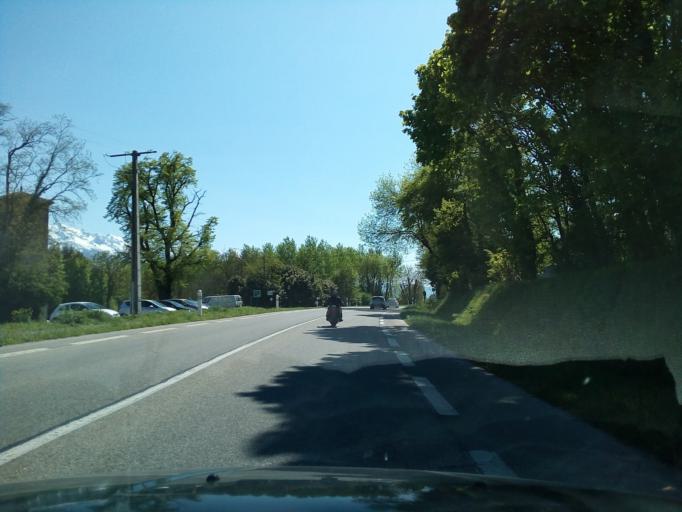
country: FR
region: Rhone-Alpes
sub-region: Departement de l'Isere
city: La Terrasse
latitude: 45.3274
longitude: 5.9370
